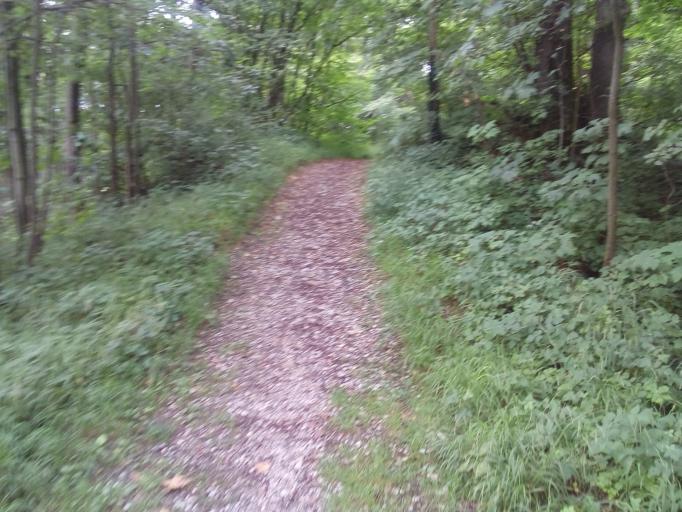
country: DE
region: Bavaria
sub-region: Upper Bavaria
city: Unterfoehring
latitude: 48.1995
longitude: 11.6406
